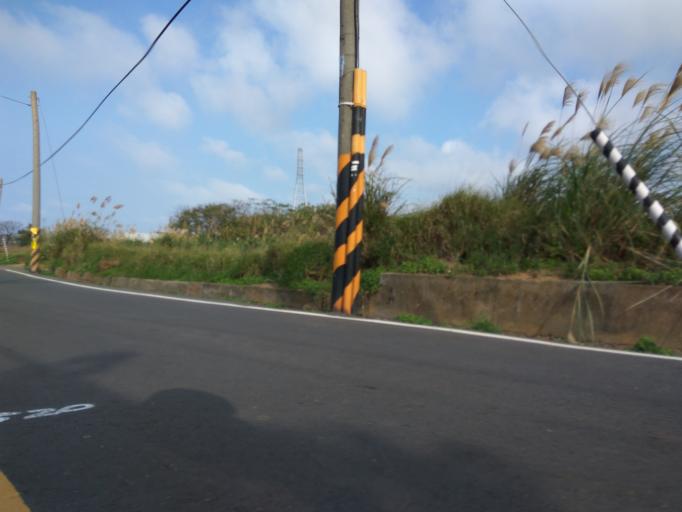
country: TW
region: Taiwan
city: Taoyuan City
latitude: 25.0659
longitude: 121.1724
